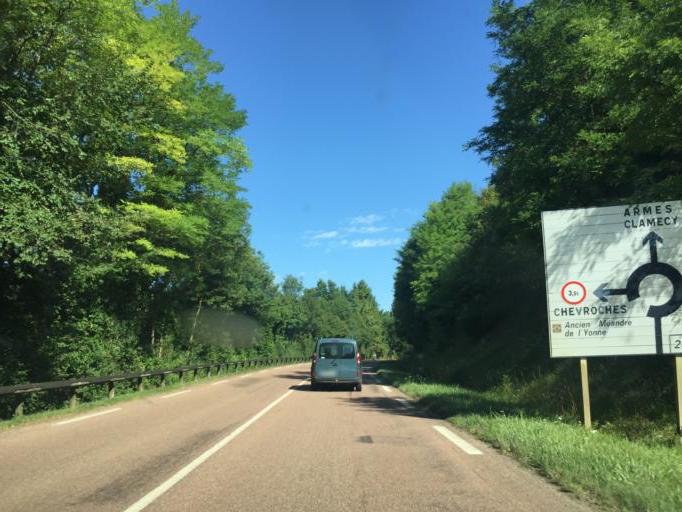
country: FR
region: Bourgogne
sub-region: Departement de la Nievre
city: Clamecy
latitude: 47.4506
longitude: 3.5520
